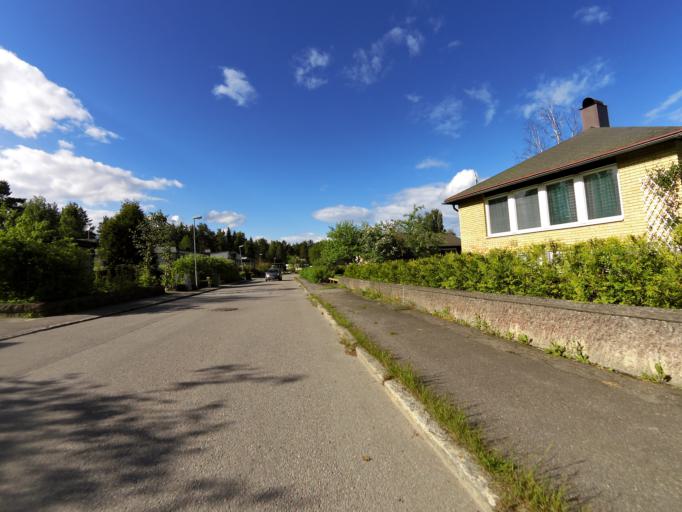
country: SE
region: Gaevleborg
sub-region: Gavle Kommun
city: Gavle
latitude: 60.6842
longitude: 17.0976
